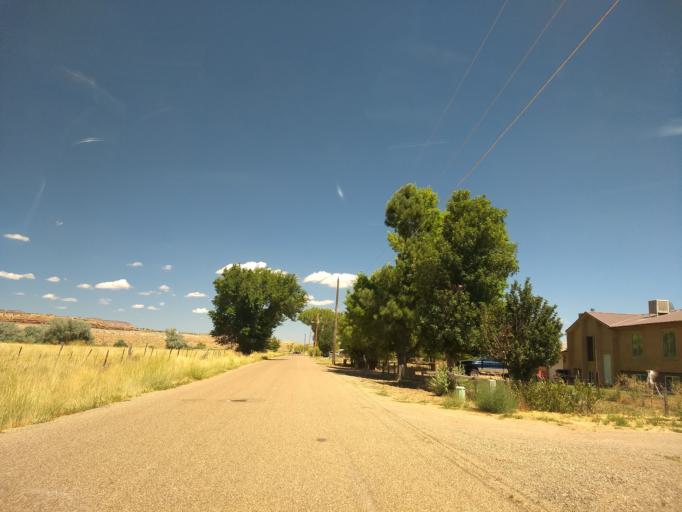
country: US
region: Arizona
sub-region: Coconino County
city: Fredonia
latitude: 36.9429
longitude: -112.5354
